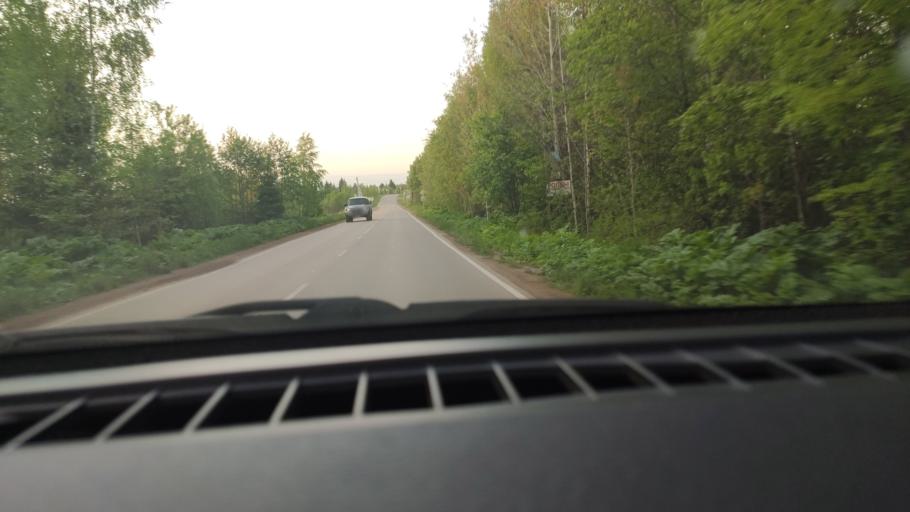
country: RU
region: Perm
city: Overyata
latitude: 58.0782
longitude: 56.0021
